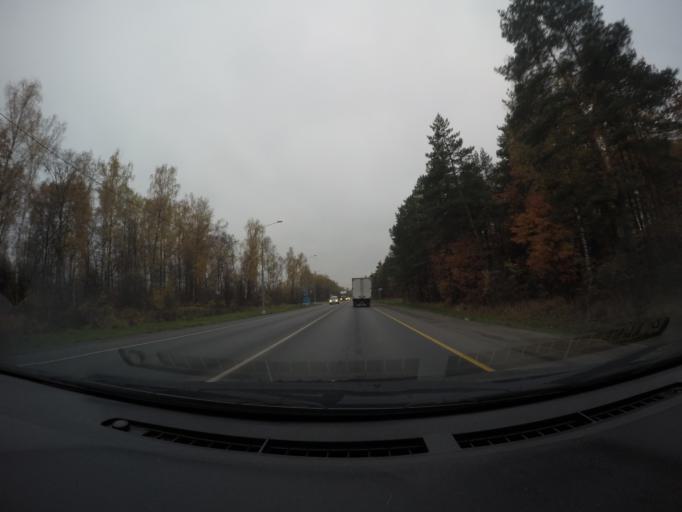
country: RU
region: Moskovskaya
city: Bronnitsy
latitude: 55.4029
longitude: 38.2280
